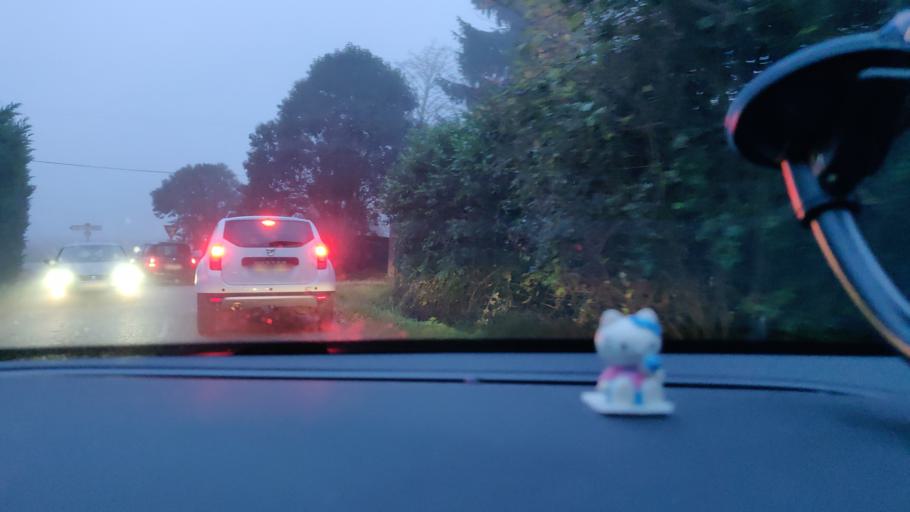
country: FR
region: Midi-Pyrenees
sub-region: Departement de la Haute-Garonne
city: Vieille-Toulouse
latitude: 43.4967
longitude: 1.4580
